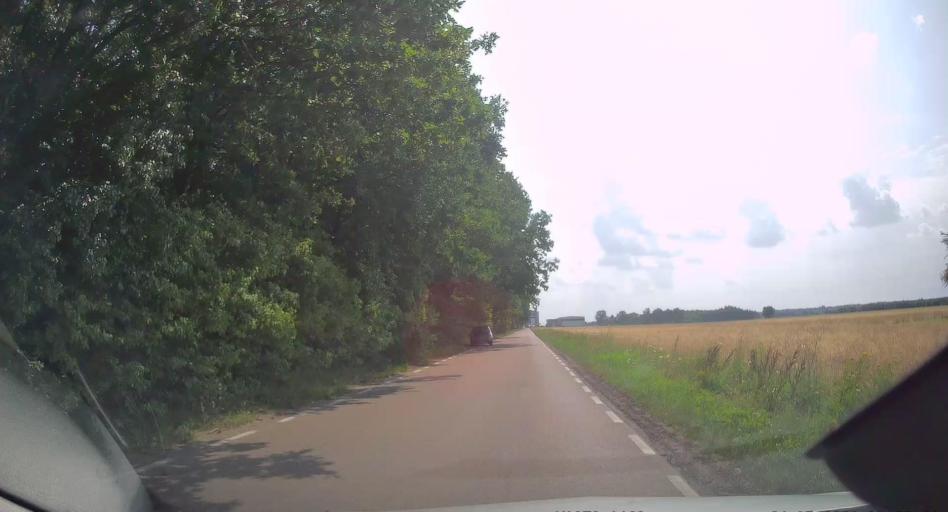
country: PL
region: Lodz Voivodeship
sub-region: Powiat tomaszowski
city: Lubochnia
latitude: 51.5755
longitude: 20.0743
